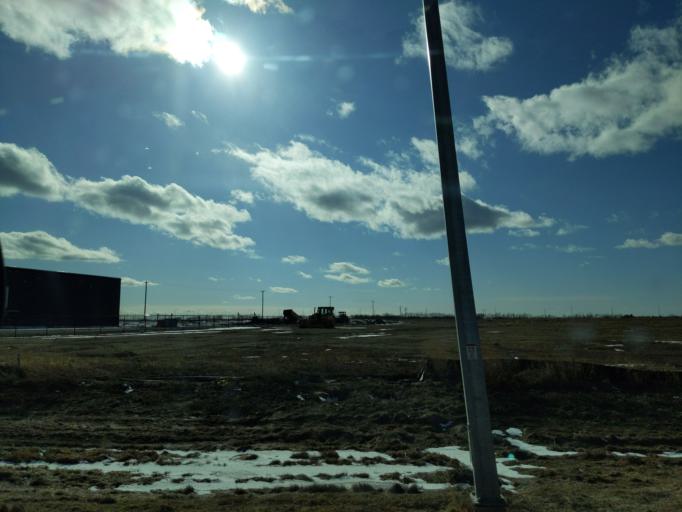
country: CA
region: Saskatchewan
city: Lloydminster
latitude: 53.3025
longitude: -110.0450
